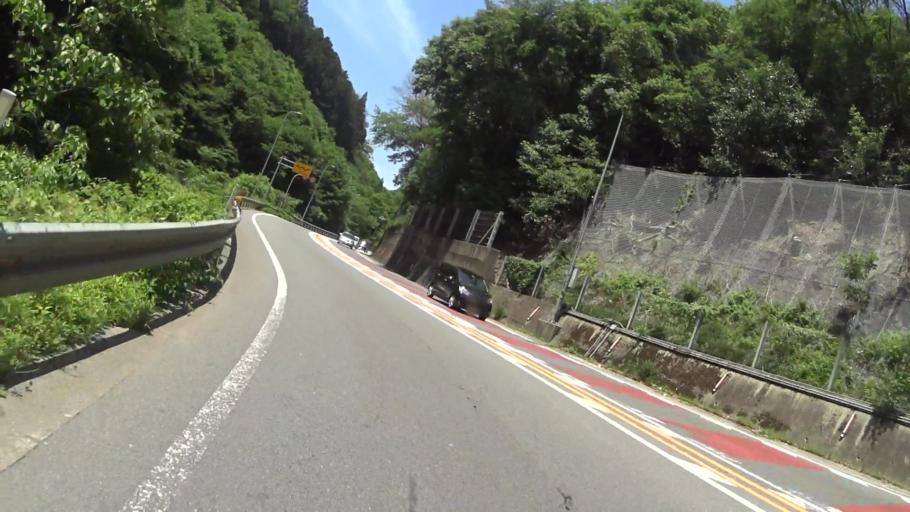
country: JP
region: Kyoto
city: Muko
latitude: 34.9920
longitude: 135.6496
